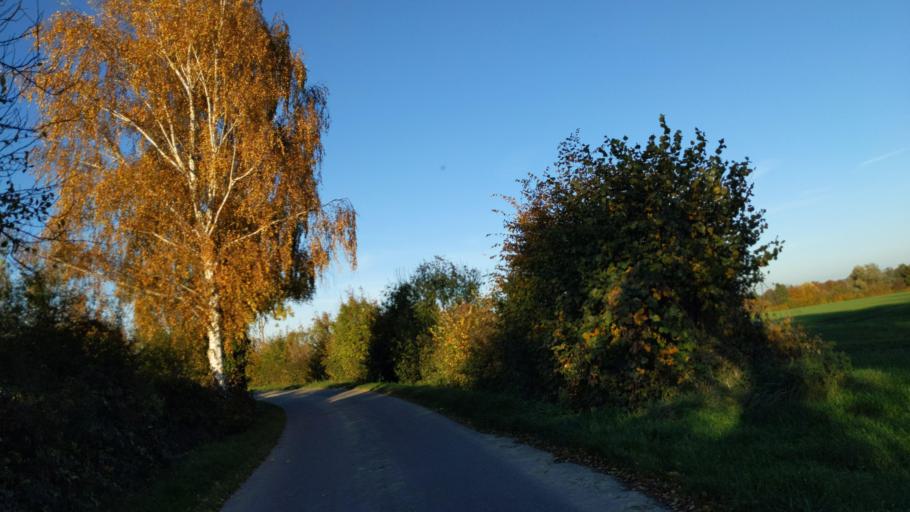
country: DE
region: Schleswig-Holstein
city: Pogeez
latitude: 53.7565
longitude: 10.7217
